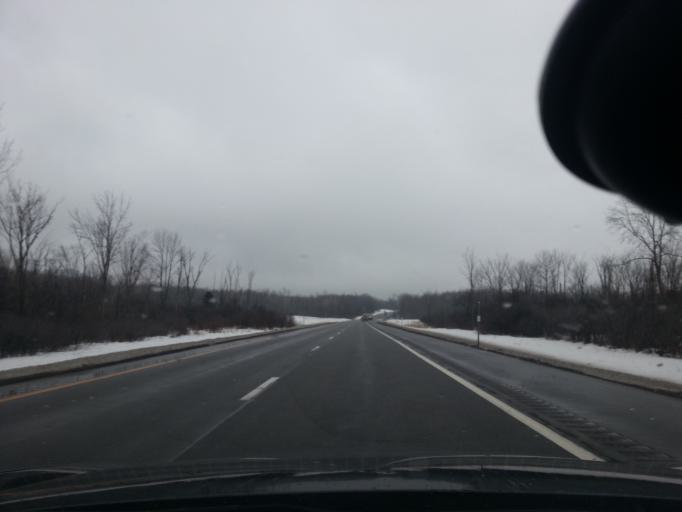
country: US
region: New York
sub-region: Oswego County
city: Pulaski
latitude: 43.6017
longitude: -76.0980
